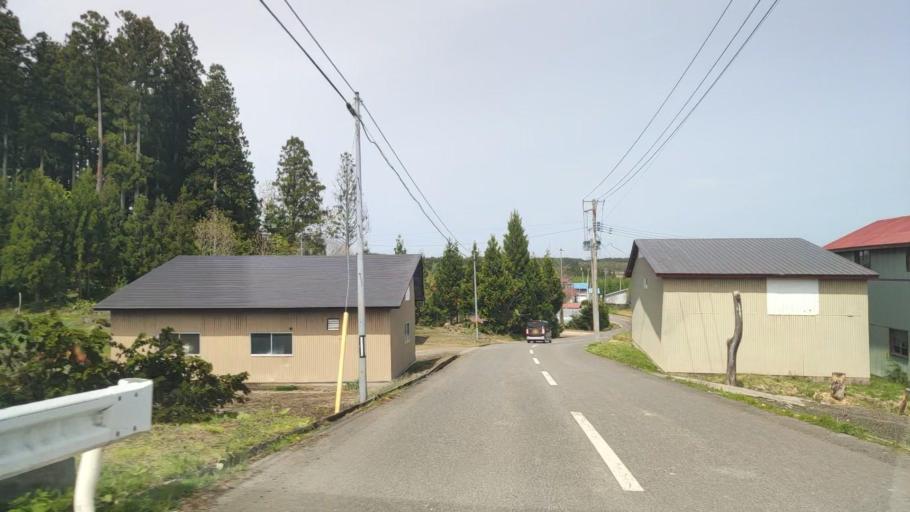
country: JP
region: Aomori
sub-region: Misawa Shi
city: Inuotose
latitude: 40.7764
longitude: 141.1217
